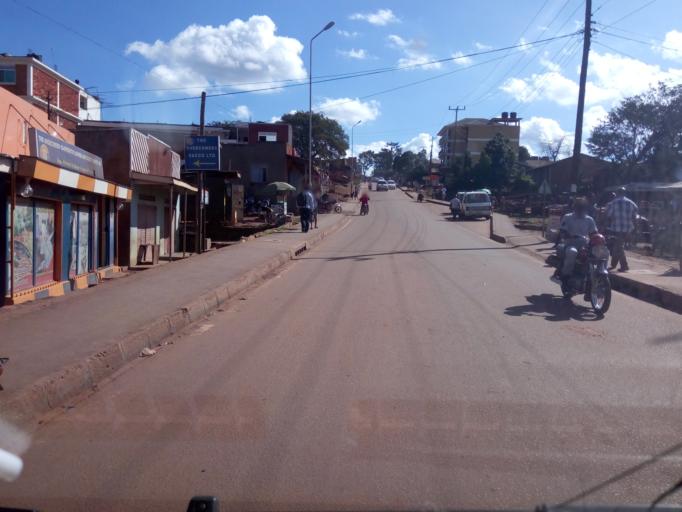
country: UG
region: Central Region
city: Kampala Central Division
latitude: 0.3332
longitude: 32.5578
